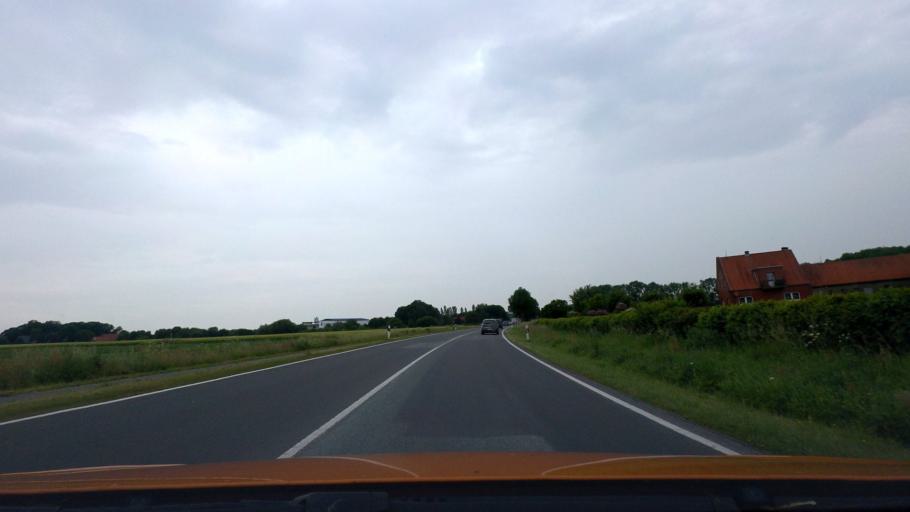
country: DE
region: Lower Saxony
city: Asendorf
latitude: 52.7617
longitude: 9.0134
